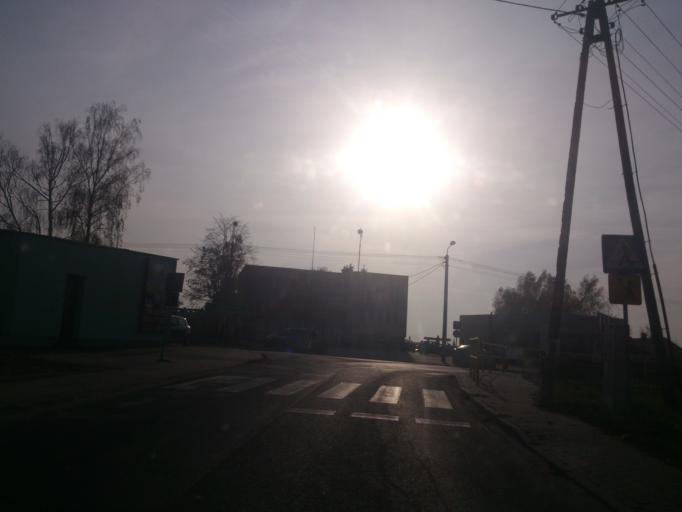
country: PL
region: Kujawsko-Pomorskie
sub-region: Powiat golubsko-dobrzynski
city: Ciechocin
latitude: 53.0571
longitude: 18.9253
